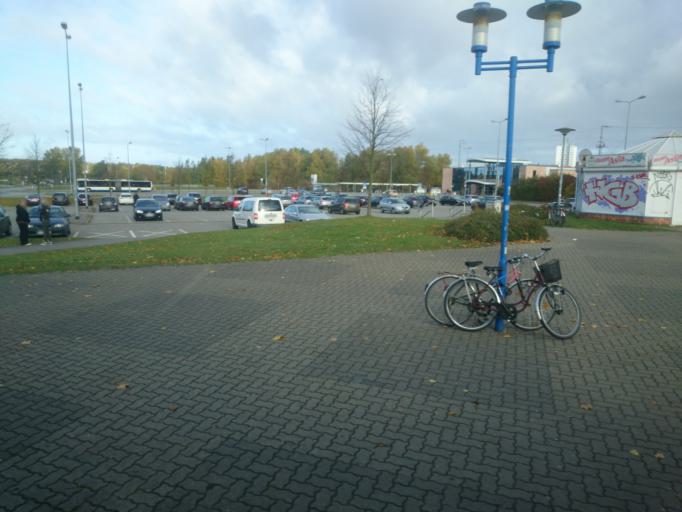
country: DE
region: Mecklenburg-Vorpommern
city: Rostock
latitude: 54.0766
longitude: 12.1300
